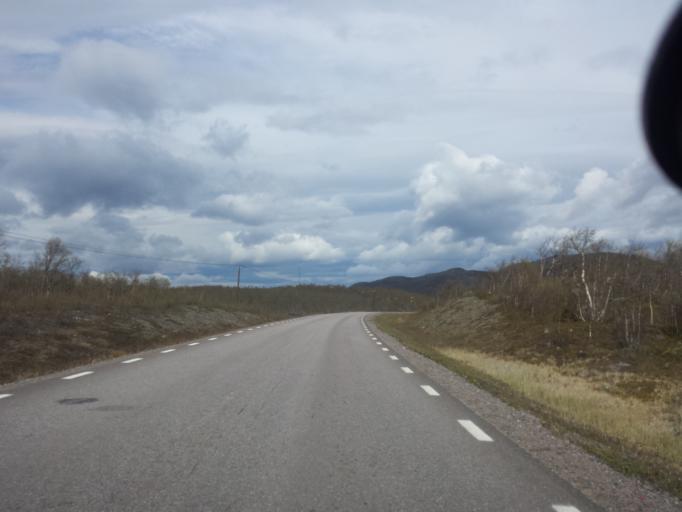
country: SE
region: Norrbotten
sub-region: Kiruna Kommun
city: Kiruna
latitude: 68.1662
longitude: 19.7860
